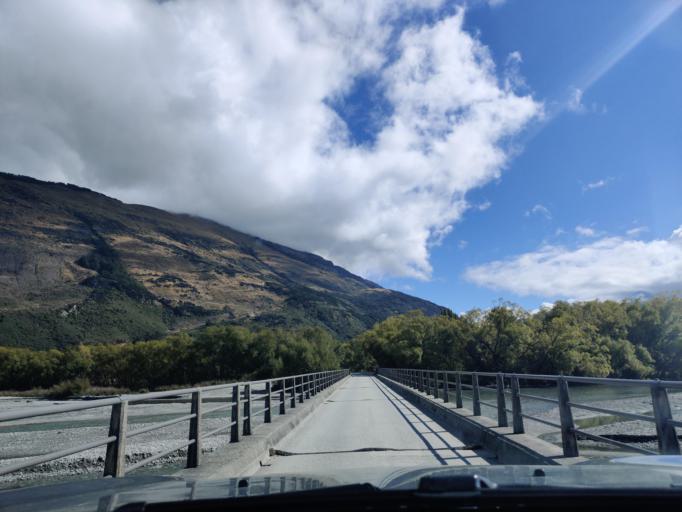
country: NZ
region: Otago
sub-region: Queenstown-Lakes District
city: Queenstown
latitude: -44.7871
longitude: 168.3966
